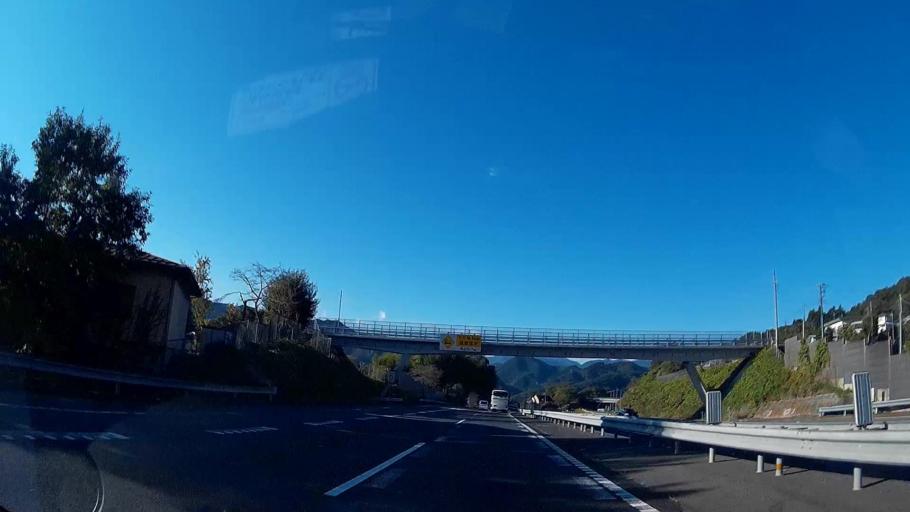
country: JP
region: Yamanashi
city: Uenohara
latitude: 35.6203
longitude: 139.1939
